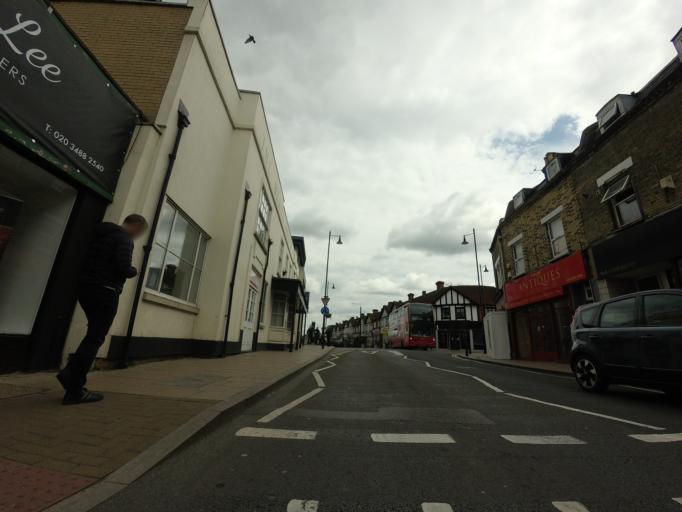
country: GB
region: England
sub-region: Greater London
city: Sidcup
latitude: 51.4252
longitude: 0.1052
